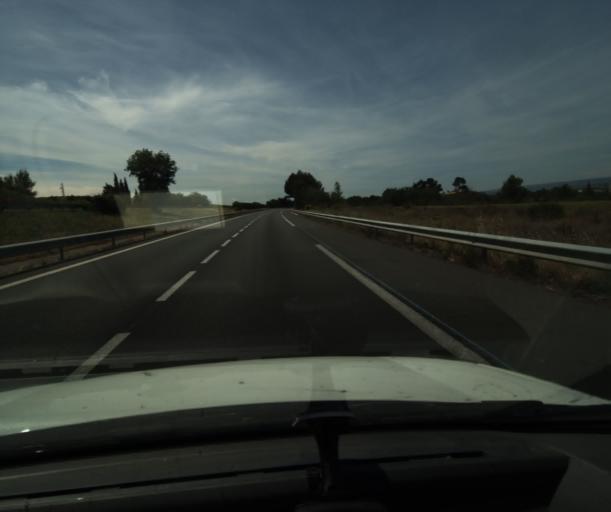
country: FR
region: Languedoc-Roussillon
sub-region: Departement de l'Aude
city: Cazilhac
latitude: 43.1915
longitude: 2.3505
